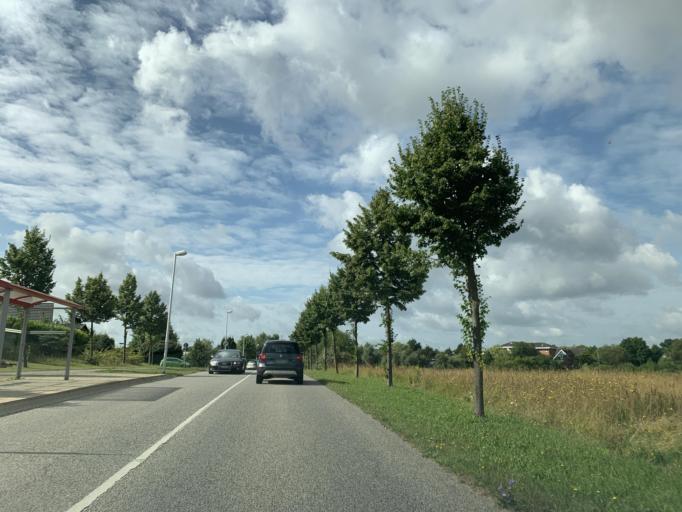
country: DE
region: Mecklenburg-Vorpommern
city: Neubrandenburg
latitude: 53.5283
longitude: 13.2701
